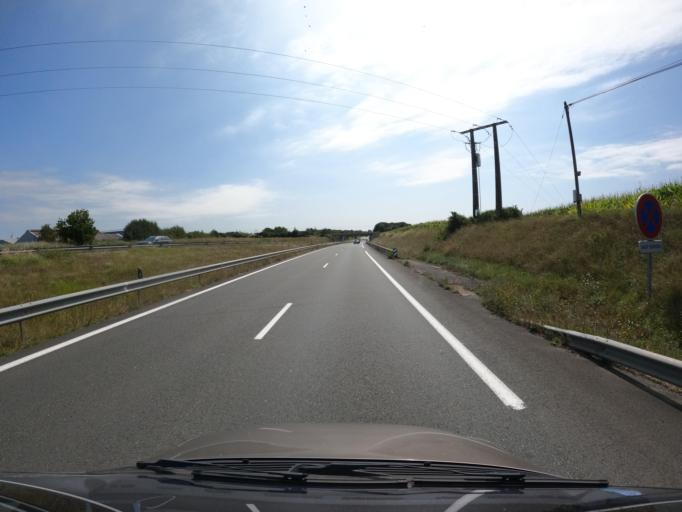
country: FR
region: Poitou-Charentes
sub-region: Departement des Deux-Sevres
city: Mauze-sur-le-Mignon
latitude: 46.1925
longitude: -0.6853
